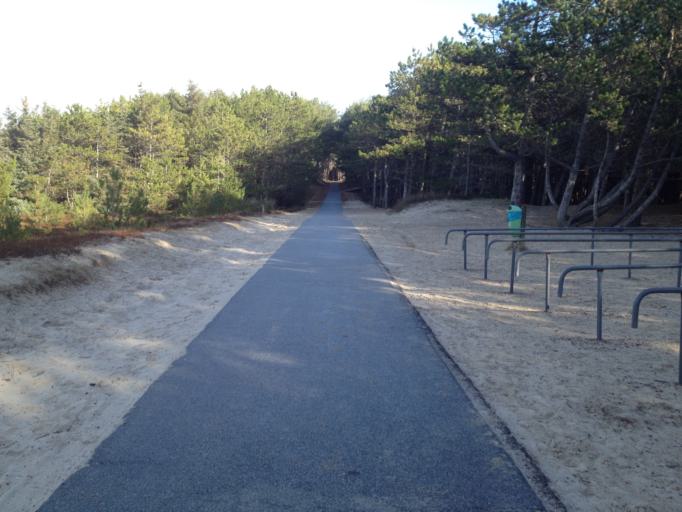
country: DE
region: Schleswig-Holstein
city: Nebel
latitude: 54.6376
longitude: 8.3393
